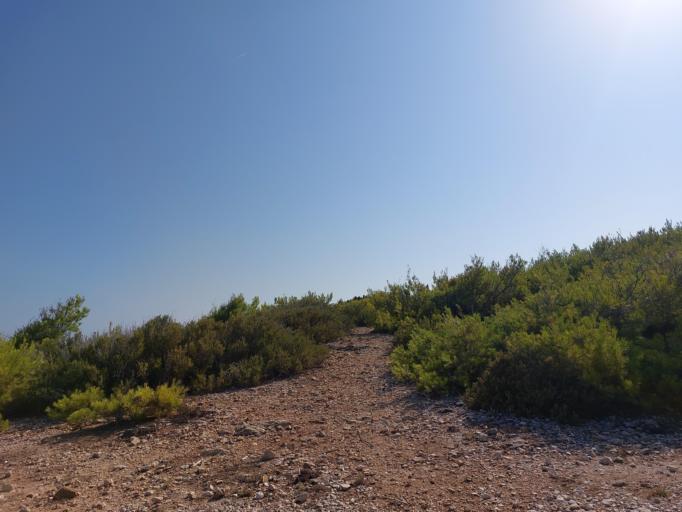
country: HR
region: Dubrovacko-Neretvanska
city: Smokvica
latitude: 42.7239
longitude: 16.8422
